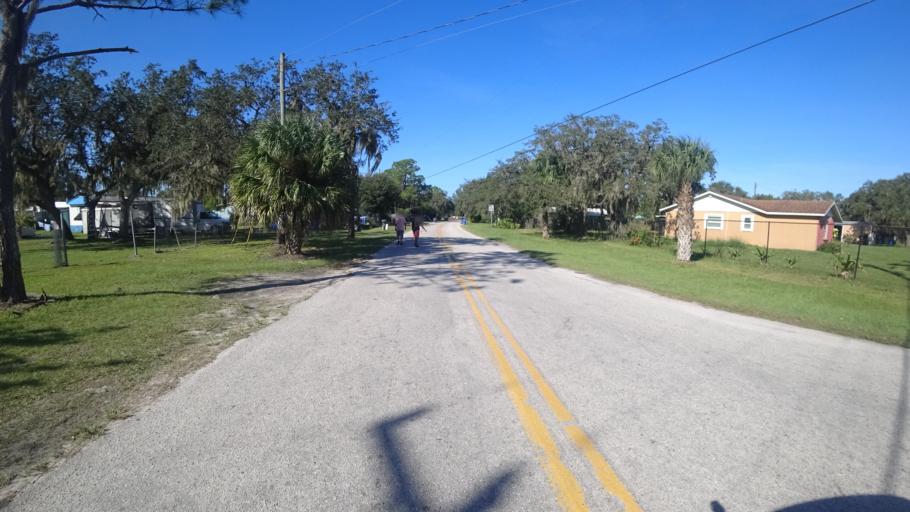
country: US
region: Florida
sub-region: Hillsborough County
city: Sun City Center
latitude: 27.6561
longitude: -82.3545
